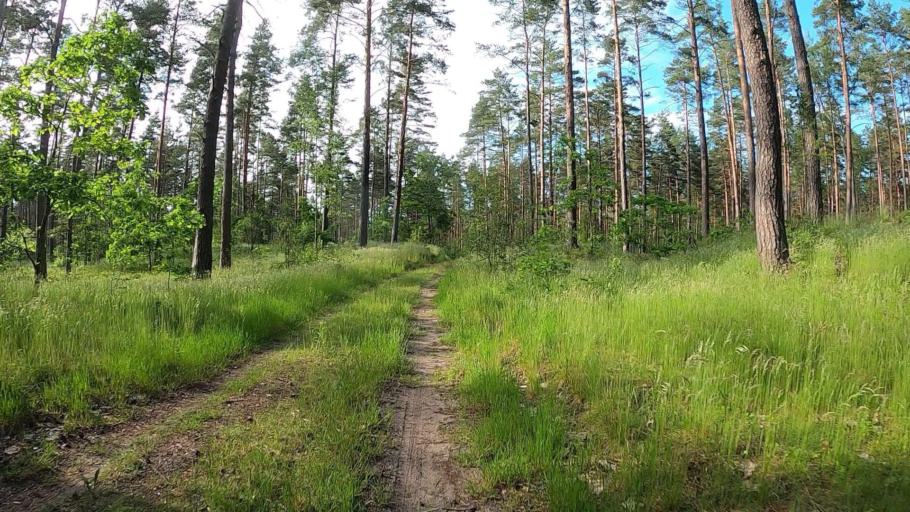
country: LV
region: Riga
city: Bergi
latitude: 57.0142
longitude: 24.2431
